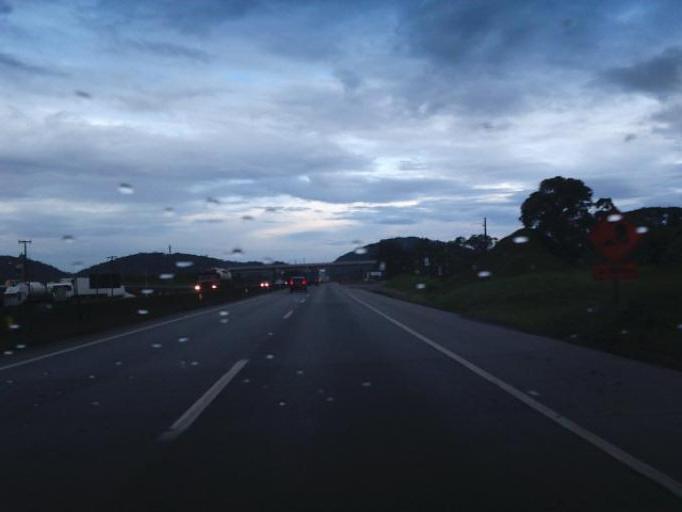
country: BR
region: Santa Catarina
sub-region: Joinville
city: Joinville
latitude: -26.0639
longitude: -48.8603
